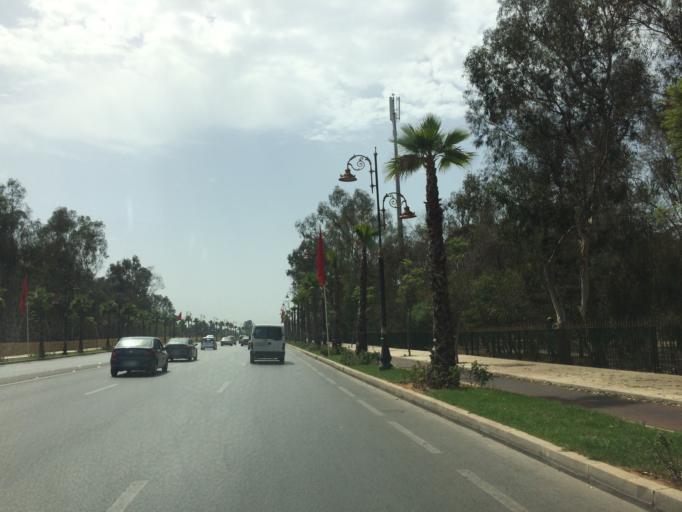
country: MA
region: Rabat-Sale-Zemmour-Zaer
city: Sale
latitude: 34.0334
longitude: -6.7784
